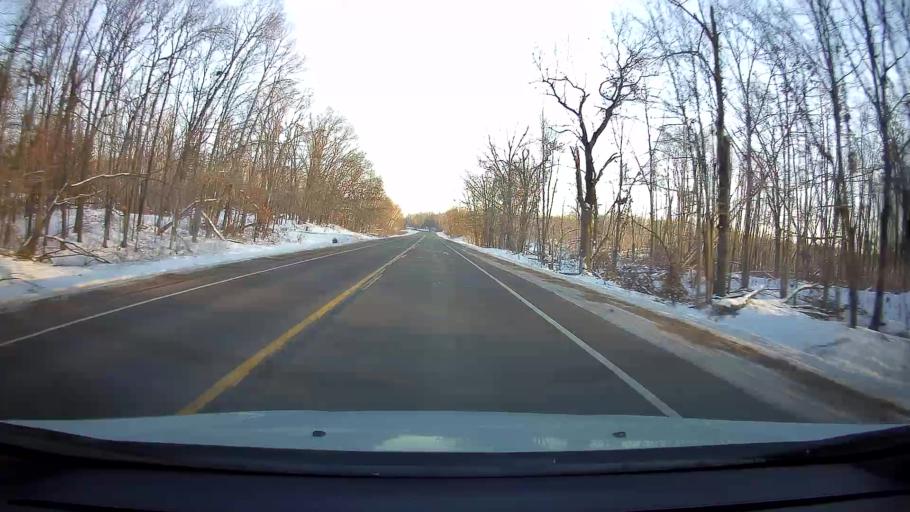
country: US
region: Wisconsin
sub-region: Barron County
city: Turtle Lake
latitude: 45.4153
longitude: -92.1327
